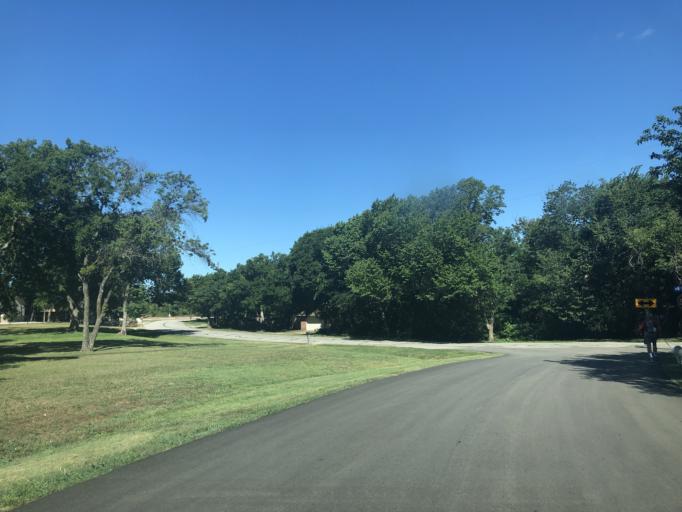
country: US
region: Texas
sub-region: Dallas County
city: Duncanville
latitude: 32.6511
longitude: -96.9413
